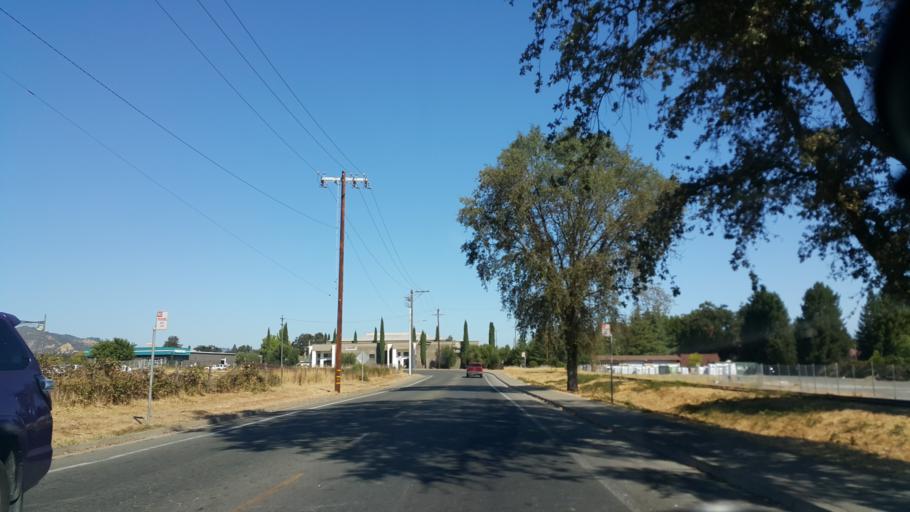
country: US
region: California
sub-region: Mendocino County
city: Ukiah
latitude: 39.1328
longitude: -123.2006
